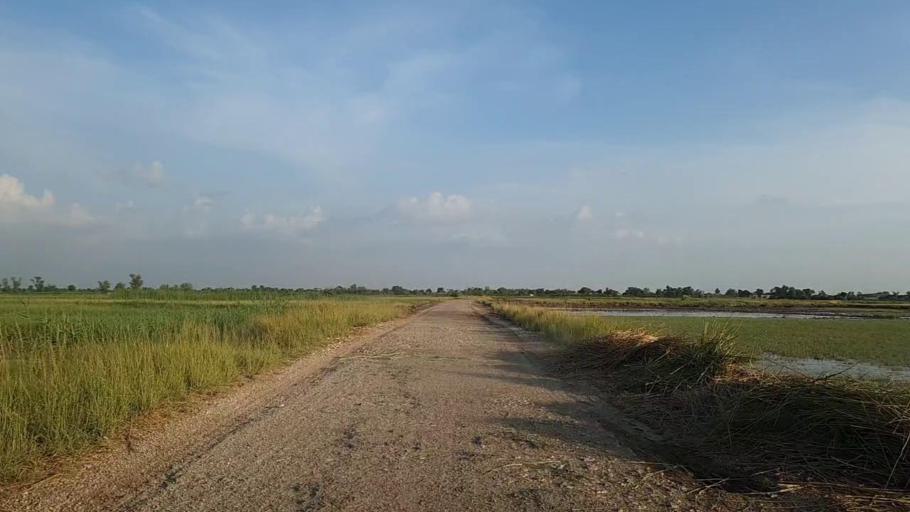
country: PK
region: Sindh
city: Karaundi
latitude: 27.0509
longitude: 68.4047
